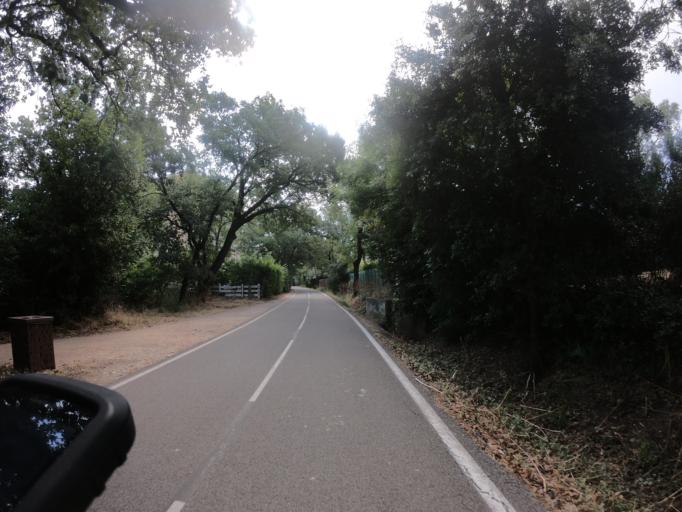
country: FR
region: Provence-Alpes-Cote d'Azur
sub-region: Departement du Var
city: La Valette-du-Var
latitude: 43.1178
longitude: 5.9711
